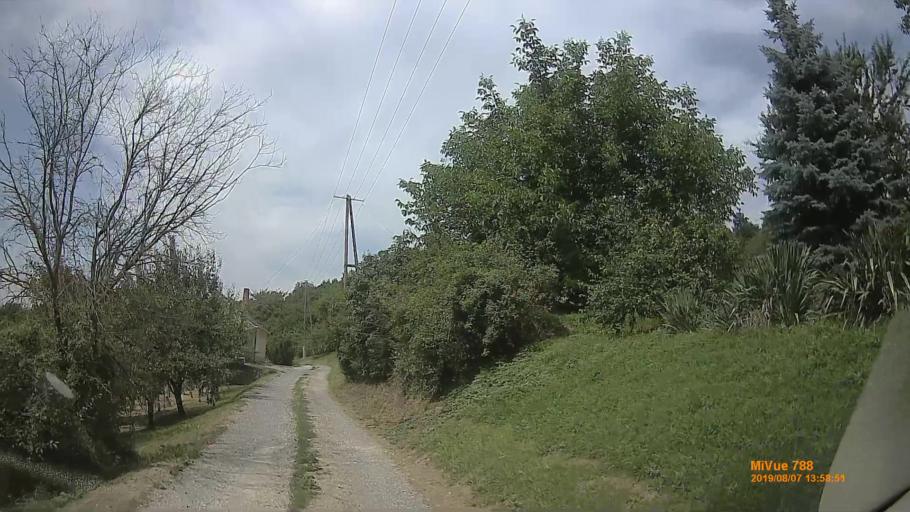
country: HU
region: Zala
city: Cserszegtomaj
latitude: 46.8977
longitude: 17.1761
